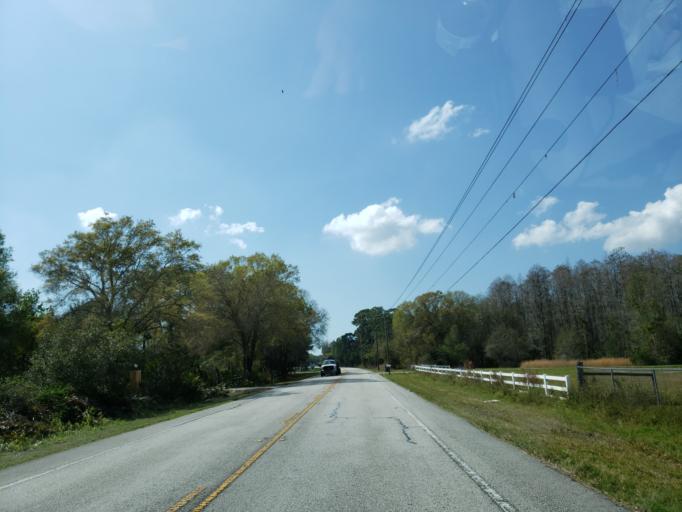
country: US
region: Florida
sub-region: Hillsborough County
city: Keystone
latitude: 28.1420
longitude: -82.6171
